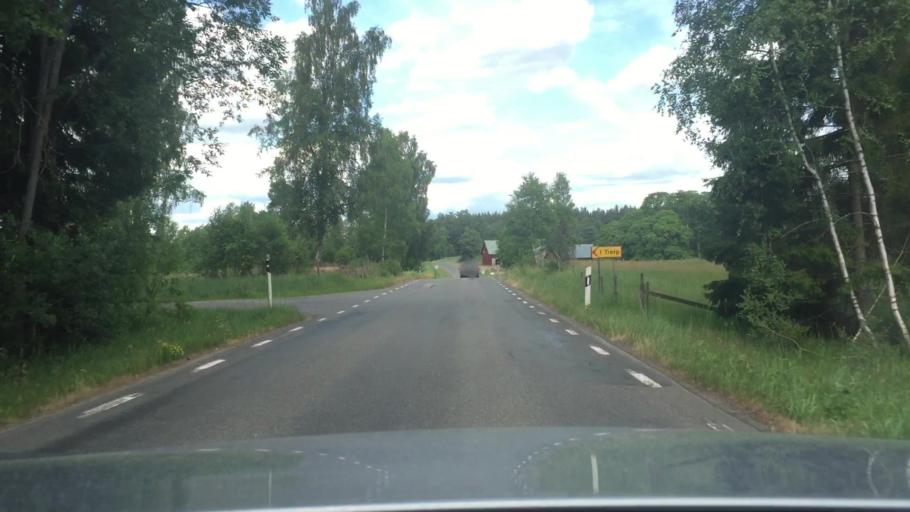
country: SE
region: Vaestra Goetaland
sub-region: Tidaholms Kommun
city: Tidaholm
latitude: 58.2064
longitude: 13.9821
